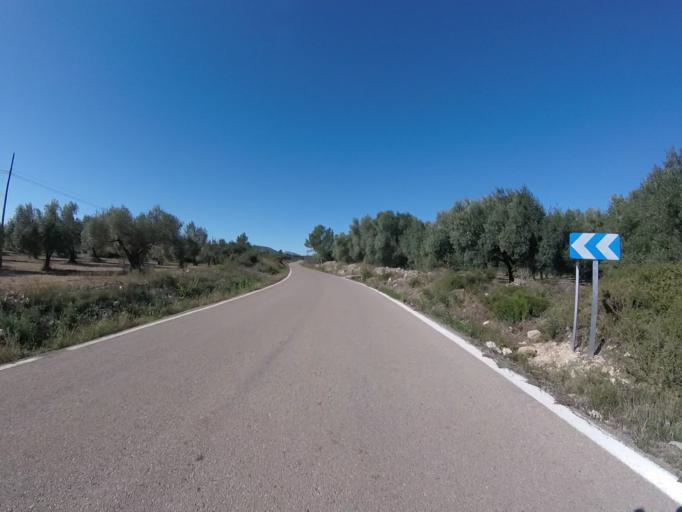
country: ES
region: Valencia
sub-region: Provincia de Castello
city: Chert/Xert
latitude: 40.4580
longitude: 0.1512
